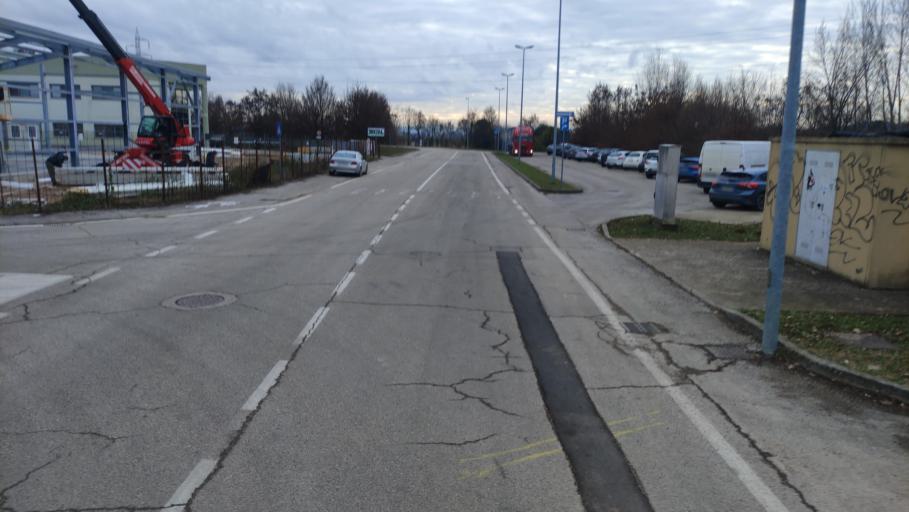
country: IT
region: Veneto
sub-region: Provincia di Vicenza
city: Villaverla
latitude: 45.6324
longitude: 11.4801
